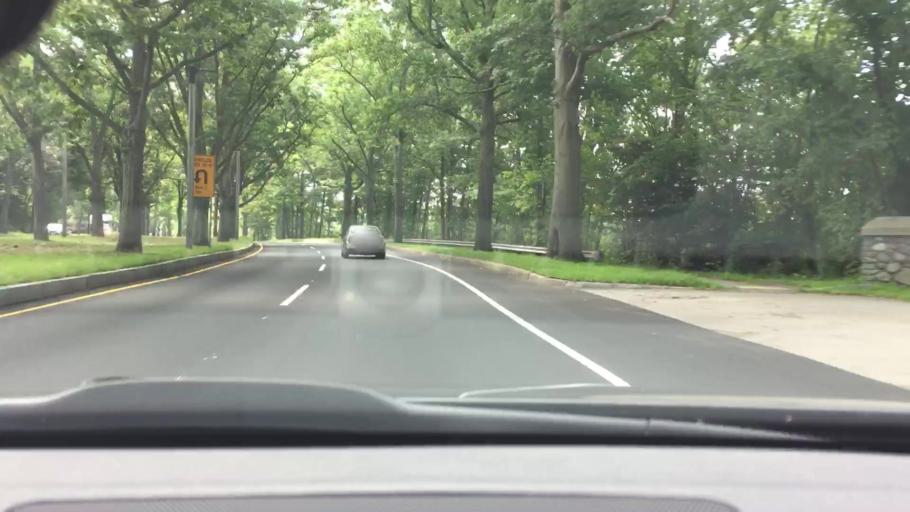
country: US
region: Massachusetts
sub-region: Norfolk County
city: Dedham
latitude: 42.2844
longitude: -71.1724
